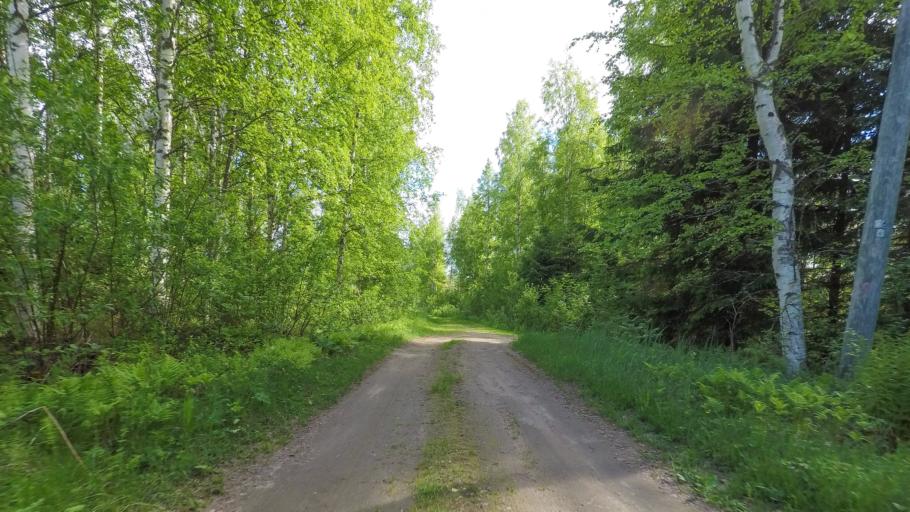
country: FI
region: Central Finland
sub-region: Jyvaeskylae
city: Hankasalmi
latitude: 62.4251
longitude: 26.6667
